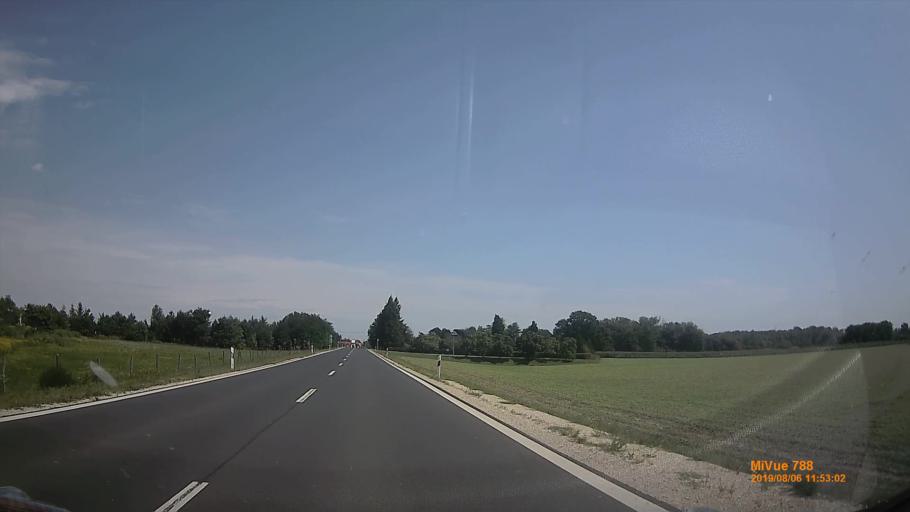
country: HU
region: Vas
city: Kormend
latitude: 47.0391
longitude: 16.6620
